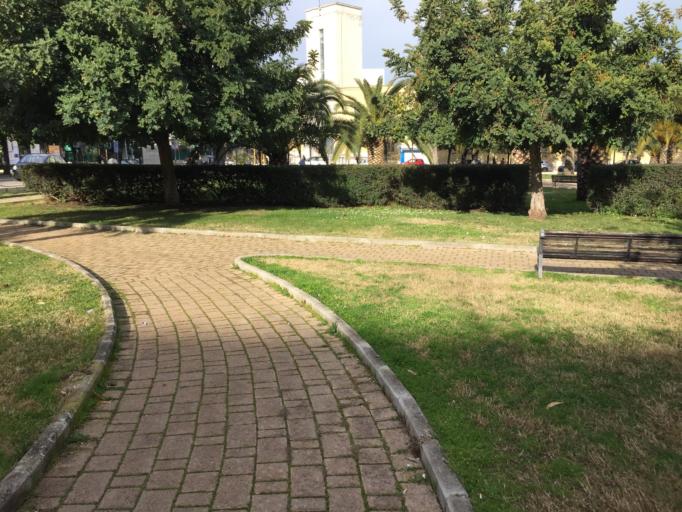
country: IT
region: Apulia
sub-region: Provincia di Barletta - Andria - Trani
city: Andria
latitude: 41.2302
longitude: 16.3039
